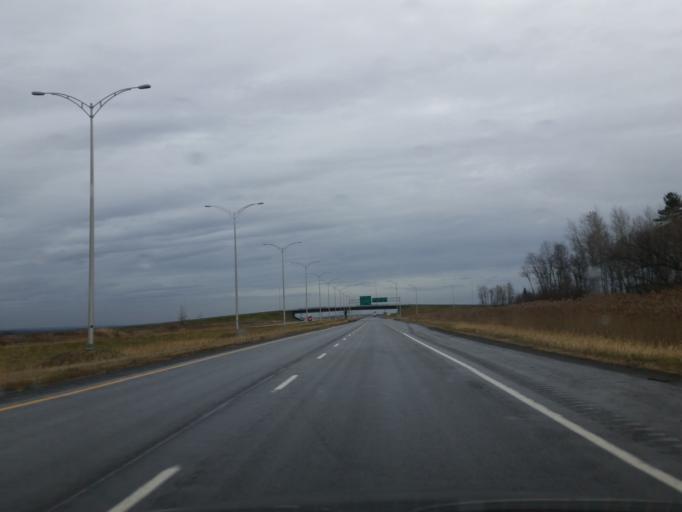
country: CA
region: Quebec
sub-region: Laurentides
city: Mirabel
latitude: 45.6948
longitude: -74.0162
